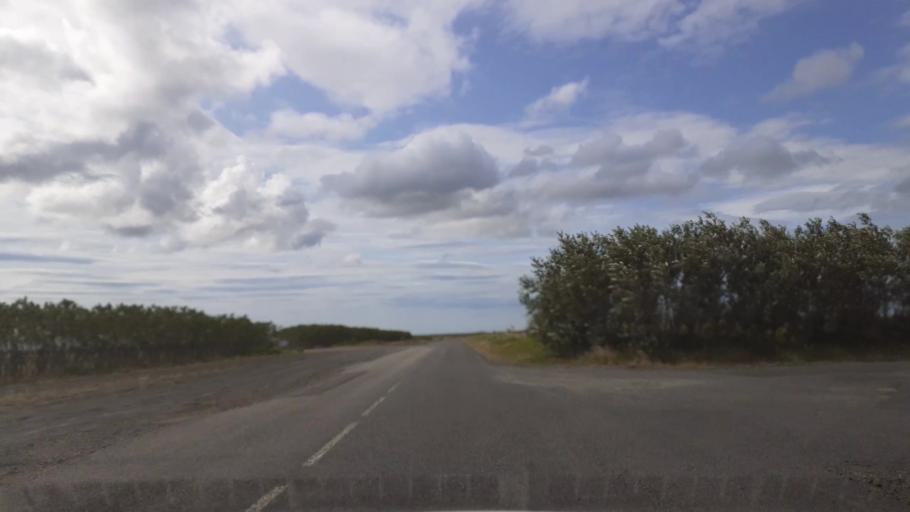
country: IS
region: South
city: Vestmannaeyjar
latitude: 63.8296
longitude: -20.4013
